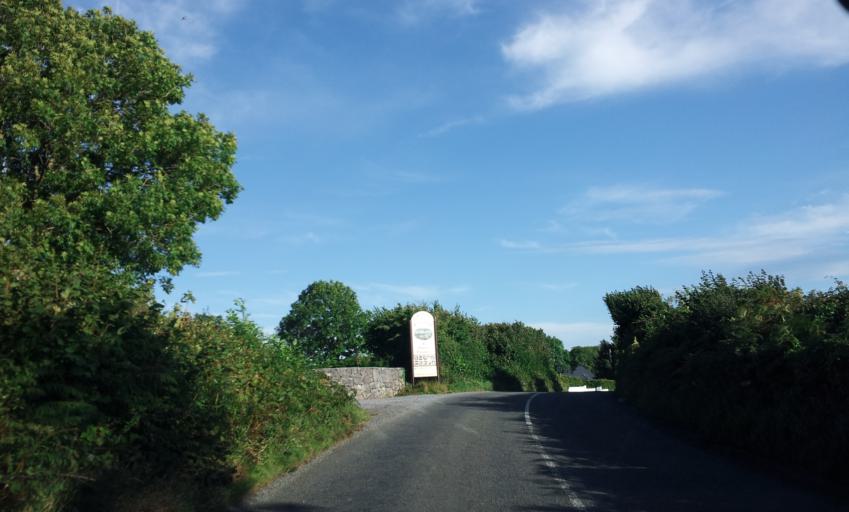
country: IE
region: Munster
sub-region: An Clar
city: Ennis
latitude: 52.9517
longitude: -9.0685
